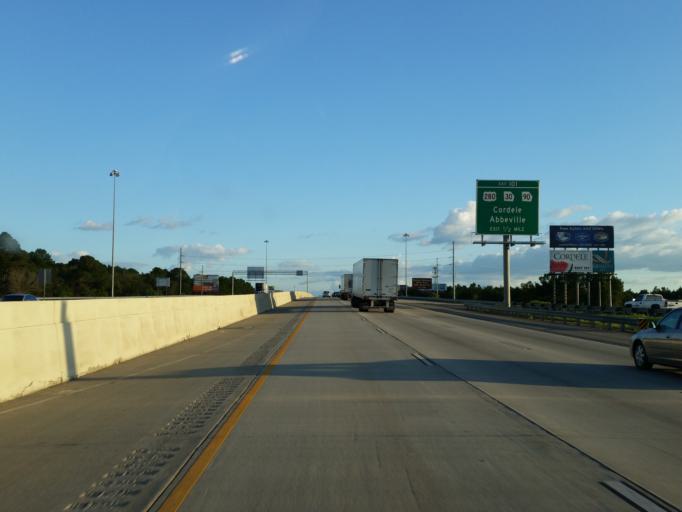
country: US
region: Georgia
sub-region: Crisp County
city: Cordele
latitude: 31.9714
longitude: -83.7532
